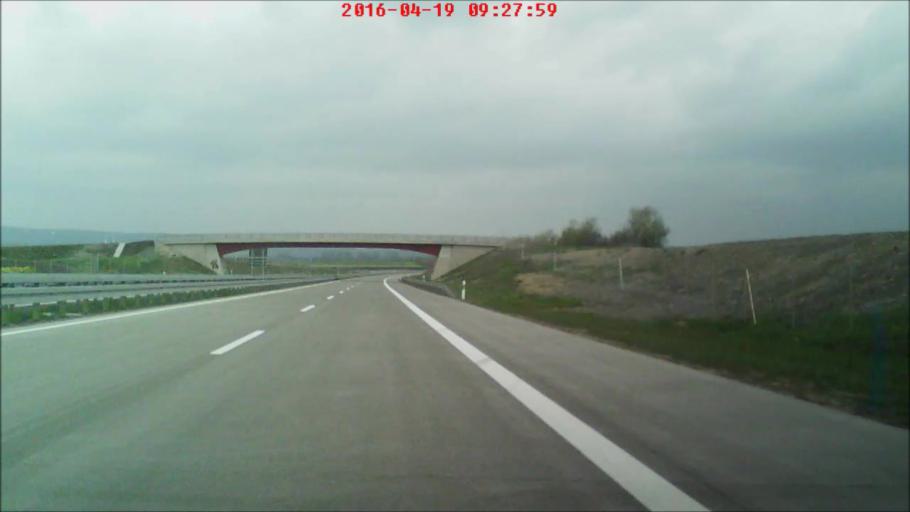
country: DE
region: Thuringia
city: Schillingstedt
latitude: 51.2251
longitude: 11.1838
